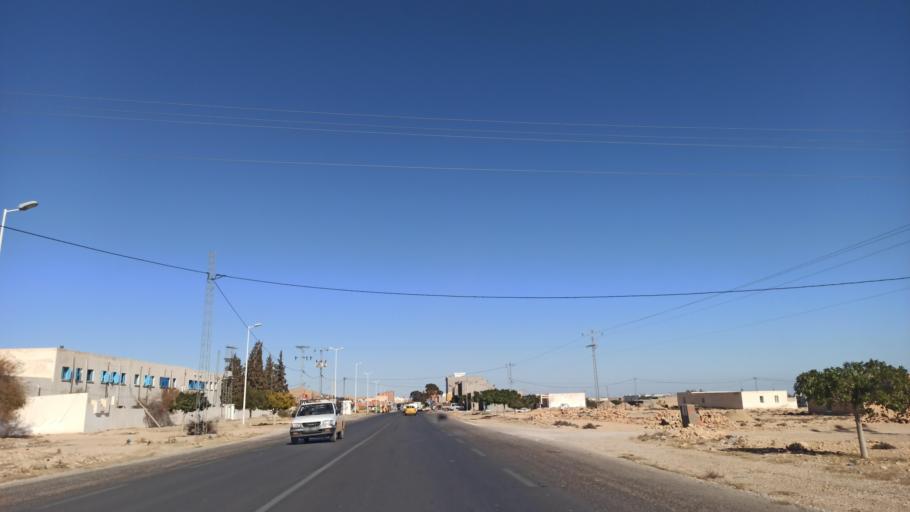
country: TN
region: Sidi Bu Zayd
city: Bi'r al Hufayy
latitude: 34.9154
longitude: 9.1844
